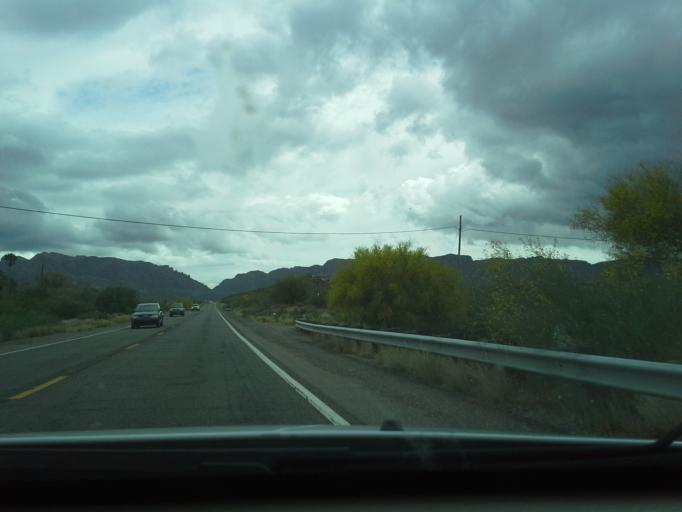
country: US
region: Arizona
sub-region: Pinal County
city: Superior
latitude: 33.2819
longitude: -111.1516
